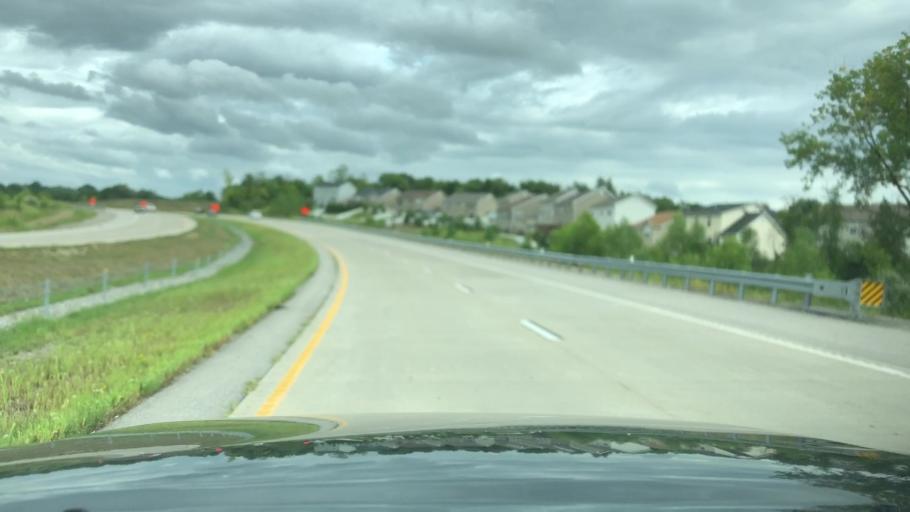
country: US
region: Missouri
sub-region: Saint Charles County
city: Cottleville
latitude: 38.7324
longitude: -90.6626
